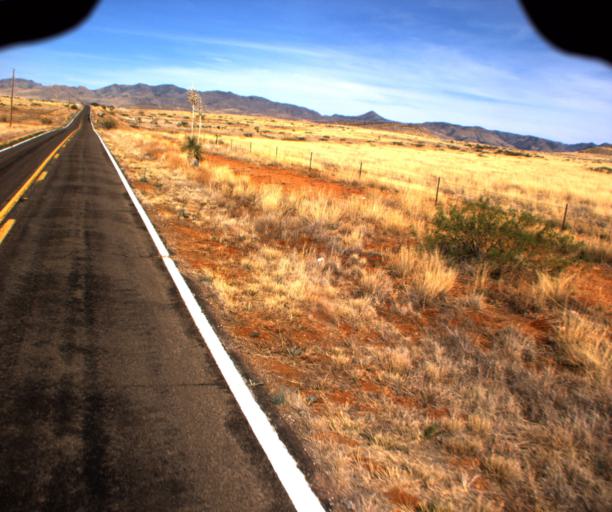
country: US
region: Arizona
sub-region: Cochise County
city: Willcox
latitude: 31.9750
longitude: -109.4689
